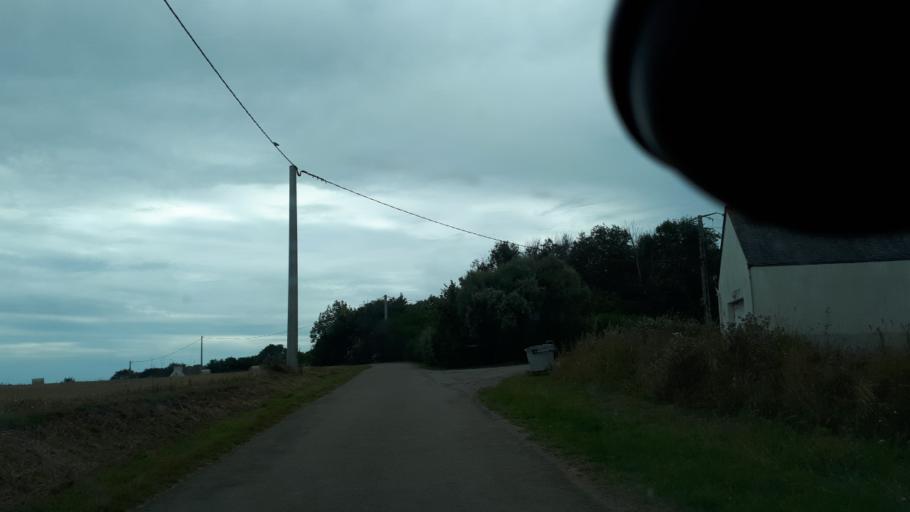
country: FR
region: Brittany
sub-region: Departement du Finistere
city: Plozevet
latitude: 47.9684
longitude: -4.3928
